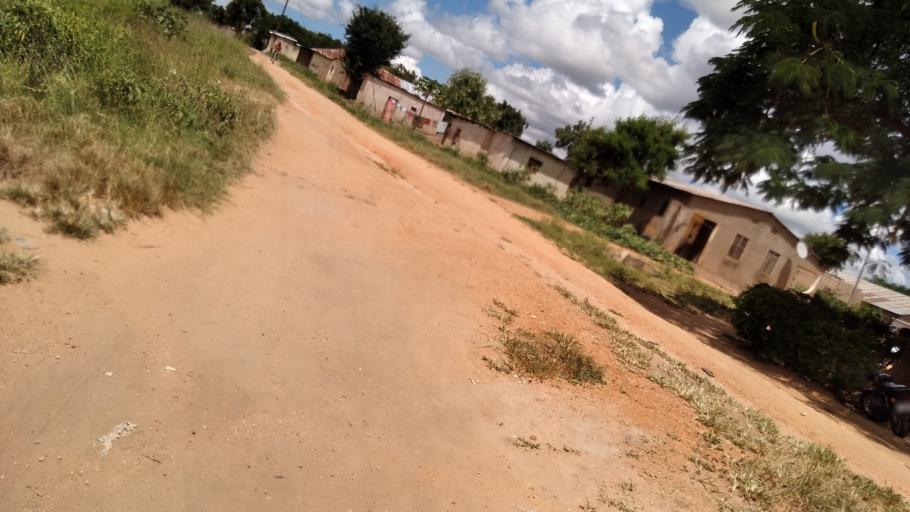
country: TZ
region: Dodoma
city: Dodoma
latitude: -6.1605
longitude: 35.7346
